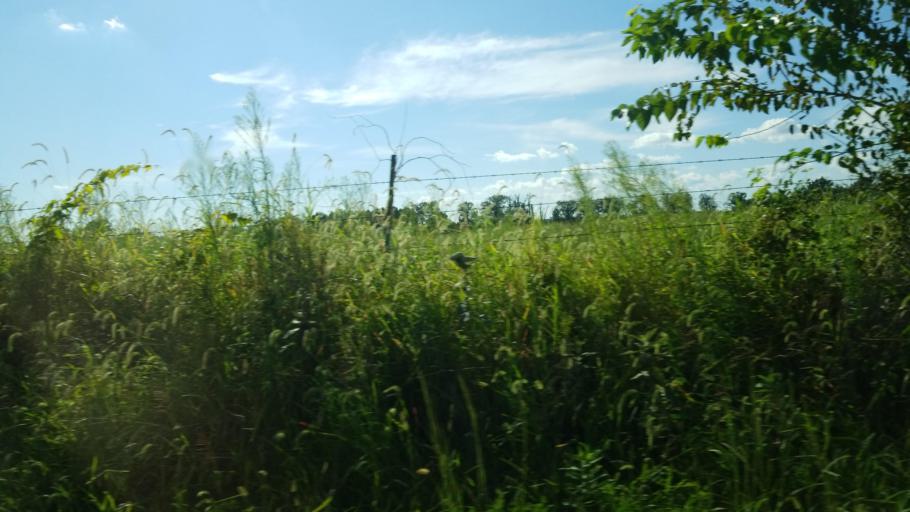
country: US
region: Illinois
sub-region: Saline County
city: Harrisburg
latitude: 37.8177
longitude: -88.5487
